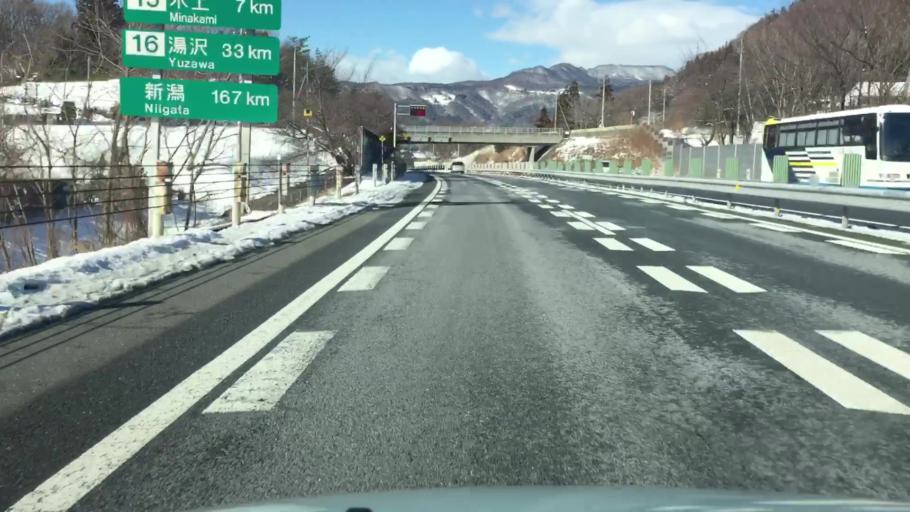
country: JP
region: Gunma
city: Numata
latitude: 36.6892
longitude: 139.0018
